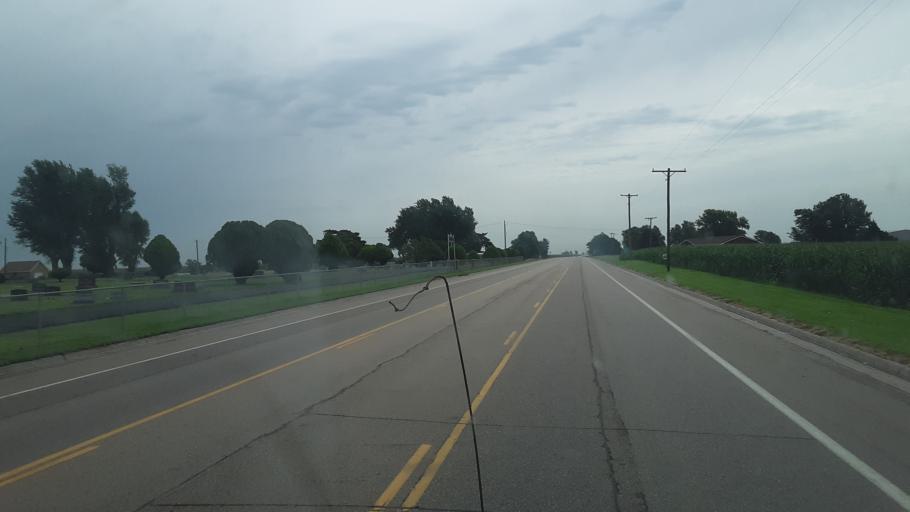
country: US
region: Kansas
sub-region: Stafford County
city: Saint John
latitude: 37.9566
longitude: -98.9607
